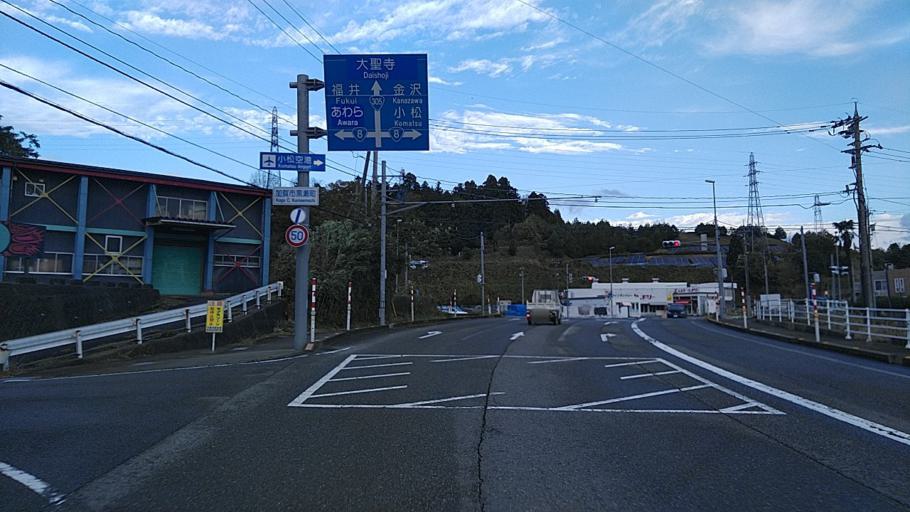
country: JP
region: Ishikawa
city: Komatsu
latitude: 36.3001
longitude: 136.3395
